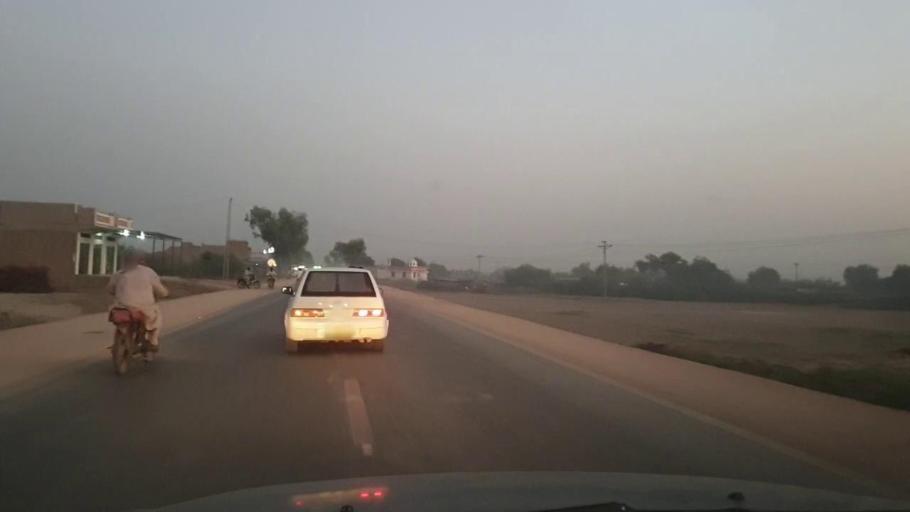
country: PK
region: Sindh
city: Tando Allahyar
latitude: 25.4346
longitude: 68.7434
